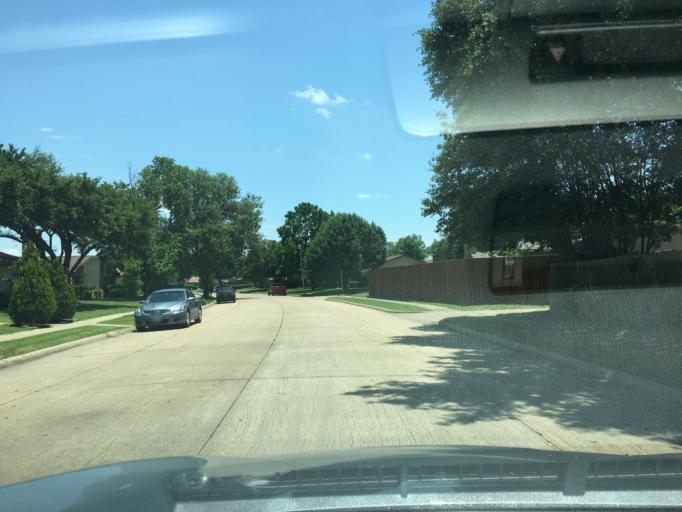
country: US
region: Texas
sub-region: Dallas County
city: Richardson
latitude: 32.9500
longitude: -96.6788
